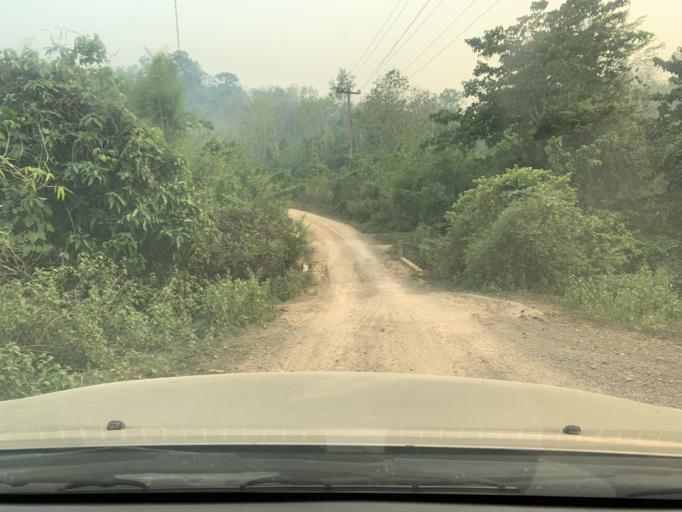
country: LA
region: Louangphabang
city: Louangphabang
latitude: 19.9251
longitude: 102.0745
